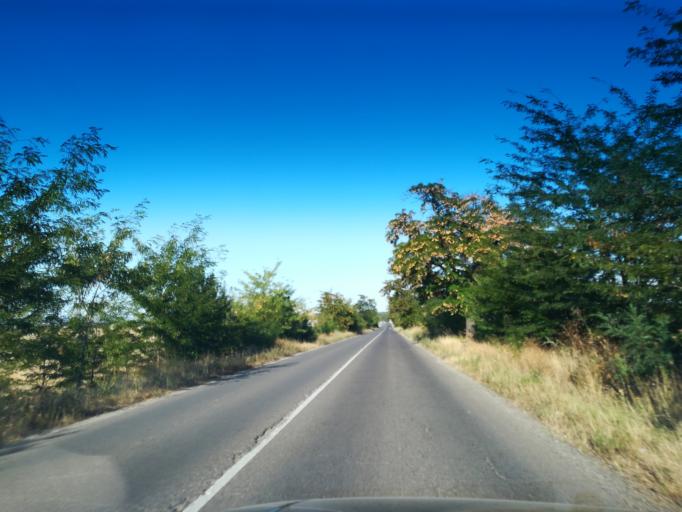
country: BG
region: Stara Zagora
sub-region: Obshtina Chirpan
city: Chirpan
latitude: 42.1745
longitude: 25.1983
